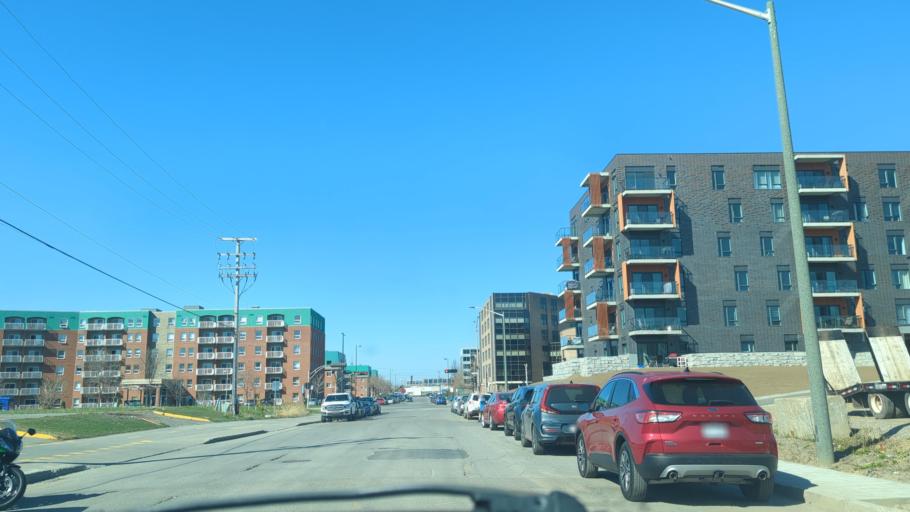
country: CA
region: Quebec
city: Quebec
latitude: 46.8467
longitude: -71.2662
